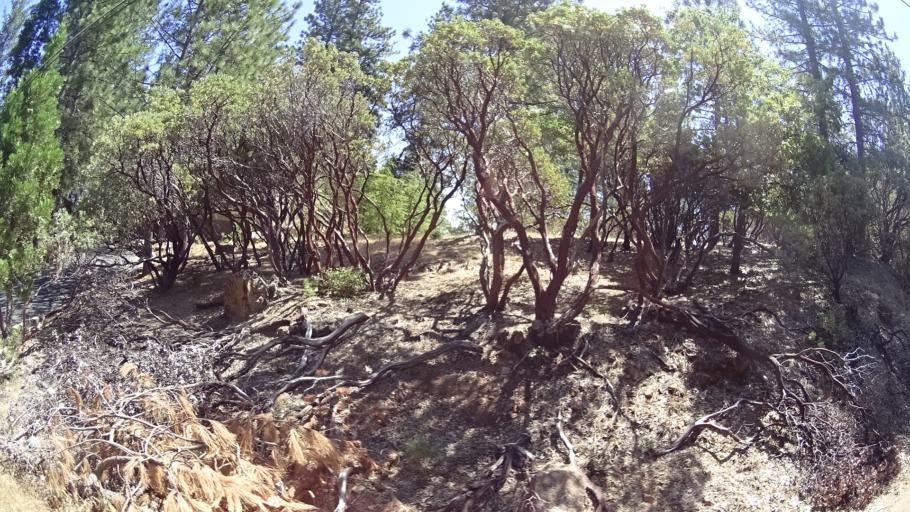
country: US
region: California
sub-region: Calaveras County
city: Arnold
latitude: 38.2259
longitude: -120.3771
